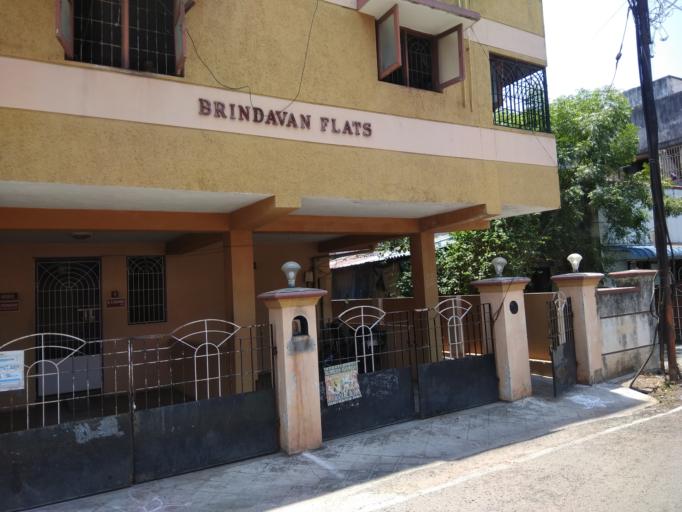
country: IN
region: Tamil Nadu
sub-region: Kancheepuram
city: Alandur
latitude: 12.9943
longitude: 80.2054
